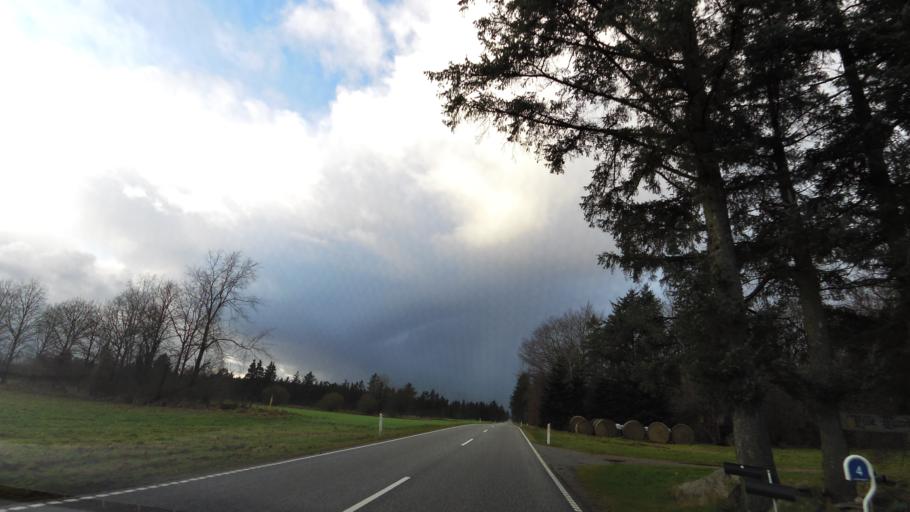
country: DK
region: South Denmark
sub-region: Vejle Kommune
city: Give
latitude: 55.9842
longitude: 9.2656
